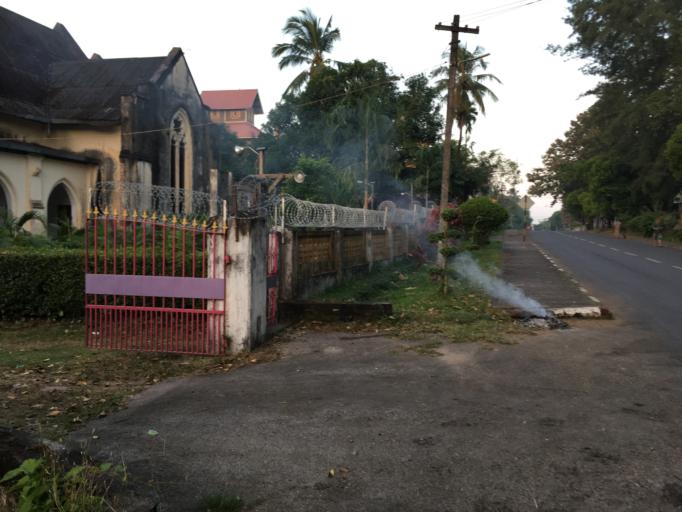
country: MM
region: Mon
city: Mawlamyine
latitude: 16.4802
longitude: 97.6236
